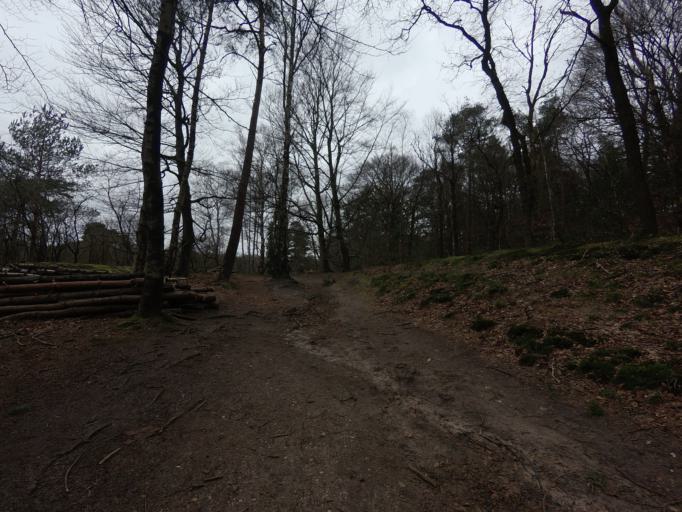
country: NL
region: Utrecht
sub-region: Gemeente Utrechtse Heuvelrug
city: Doorn
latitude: 52.0378
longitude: 5.3669
